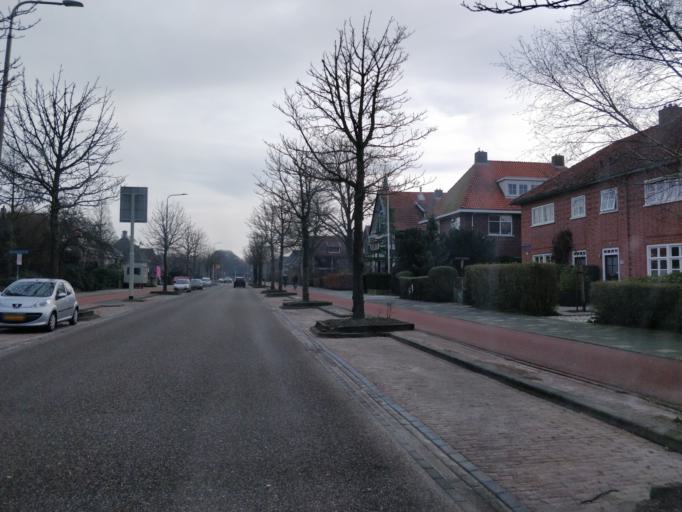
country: NL
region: Friesland
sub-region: Gemeente Leeuwarden
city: Bilgaard
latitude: 53.2047
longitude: 5.7805
